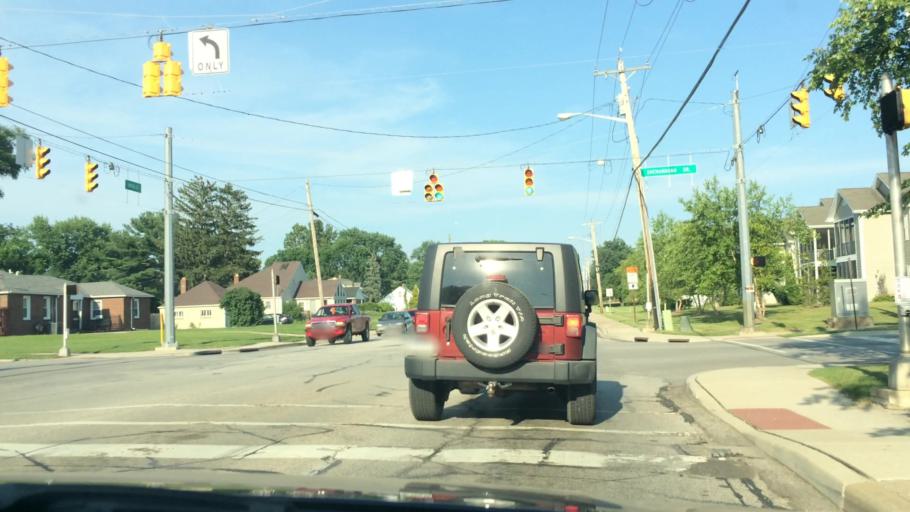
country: US
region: Indiana
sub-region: Tippecanoe County
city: Lafayette
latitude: 40.4249
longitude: -86.8474
